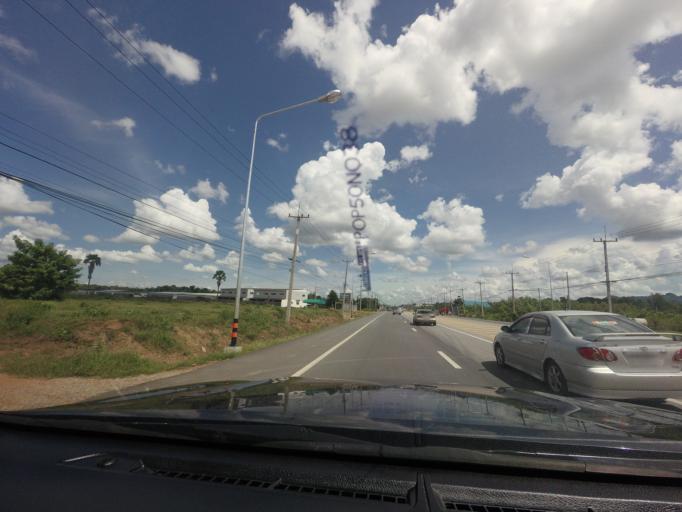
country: TH
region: Kanchanaburi
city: Kanchanaburi
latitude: 14.1077
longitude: 99.4129
